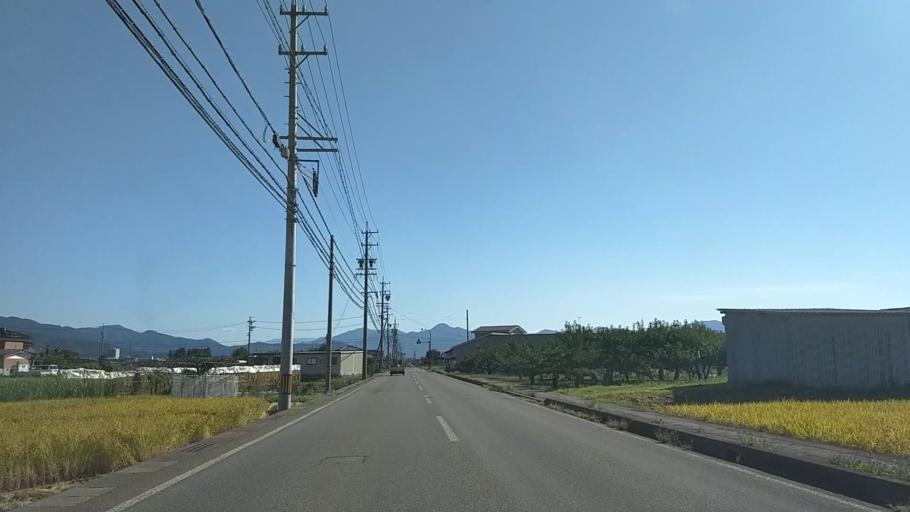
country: JP
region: Nagano
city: Nagano-shi
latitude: 36.6091
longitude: 138.1437
